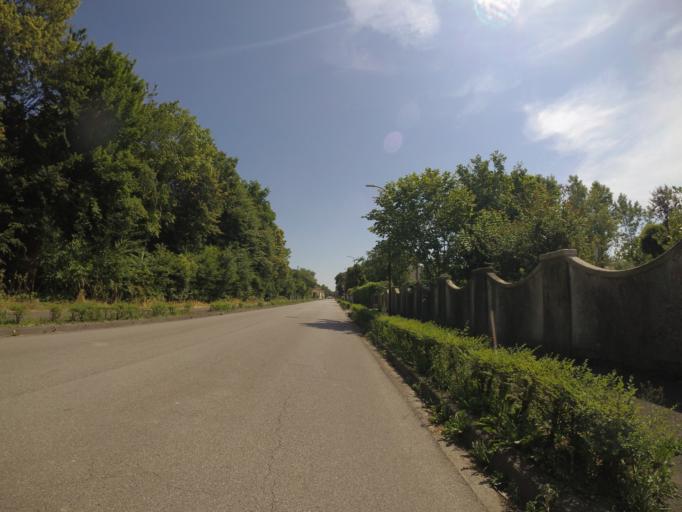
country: IT
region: Friuli Venezia Giulia
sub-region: Provincia di Udine
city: Camino al Tagliamento
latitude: 45.9302
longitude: 12.9448
